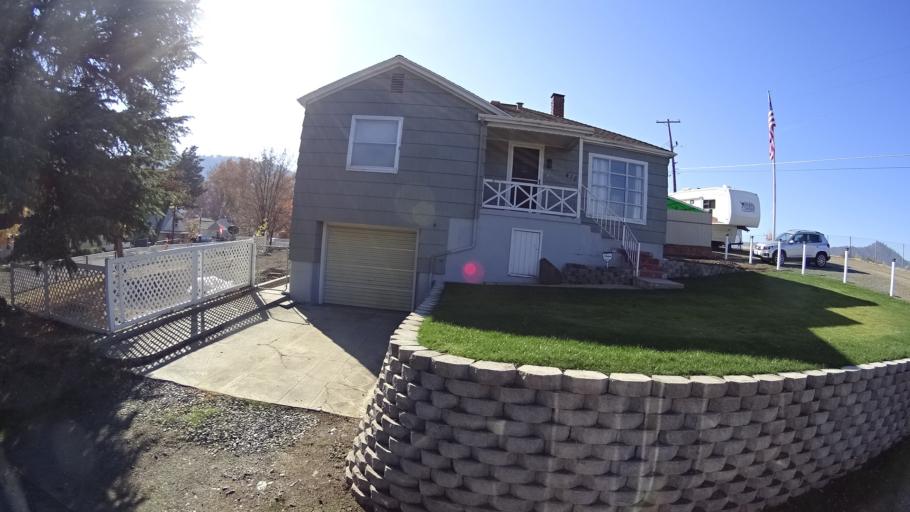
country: US
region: California
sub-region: Siskiyou County
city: Yreka
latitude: 41.7341
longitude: -122.6306
